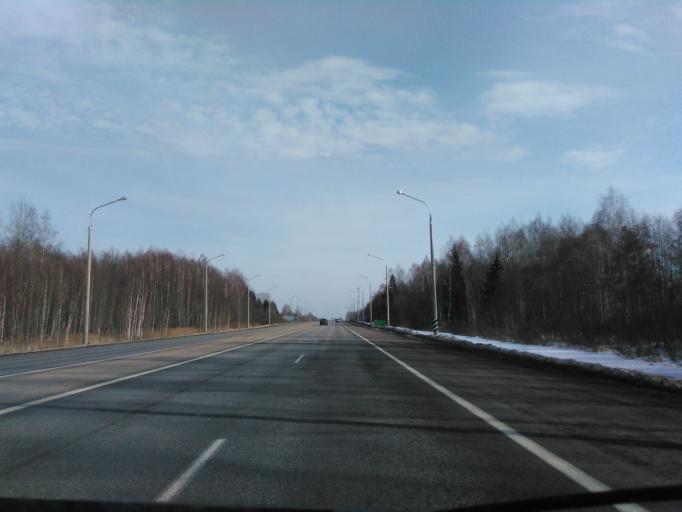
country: RU
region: Smolensk
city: Rudnya
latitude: 54.6905
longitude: 30.9740
